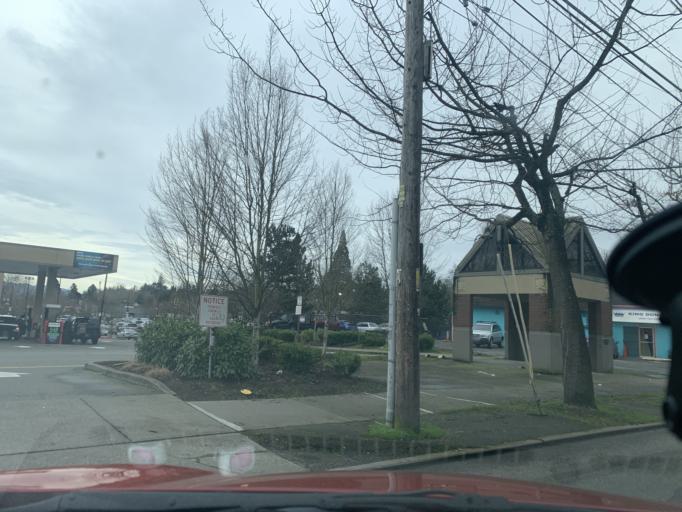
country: US
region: Washington
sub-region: King County
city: Bryn Mawr-Skyway
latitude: 47.5208
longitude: -122.2700
